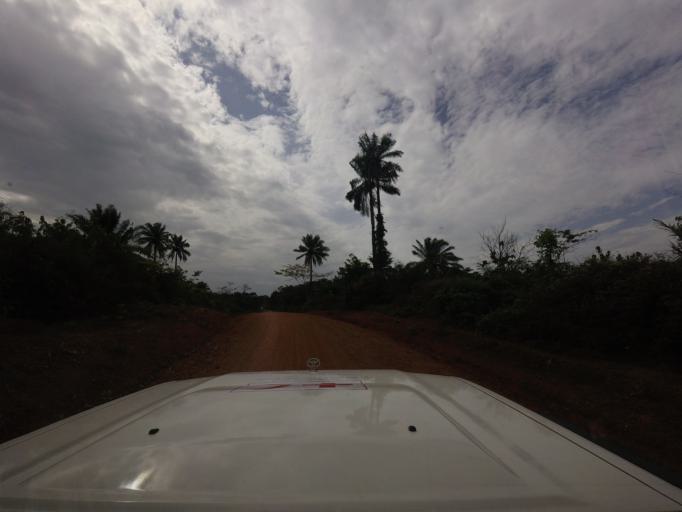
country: SL
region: Eastern Province
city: Buedu
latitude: 8.2641
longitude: -10.2358
